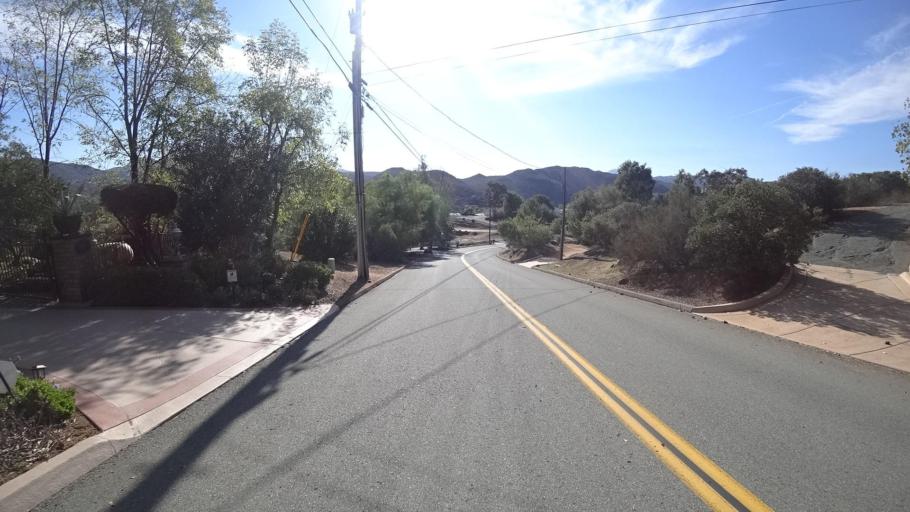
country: US
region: California
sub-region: San Diego County
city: Alpine
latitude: 32.8159
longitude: -116.7464
